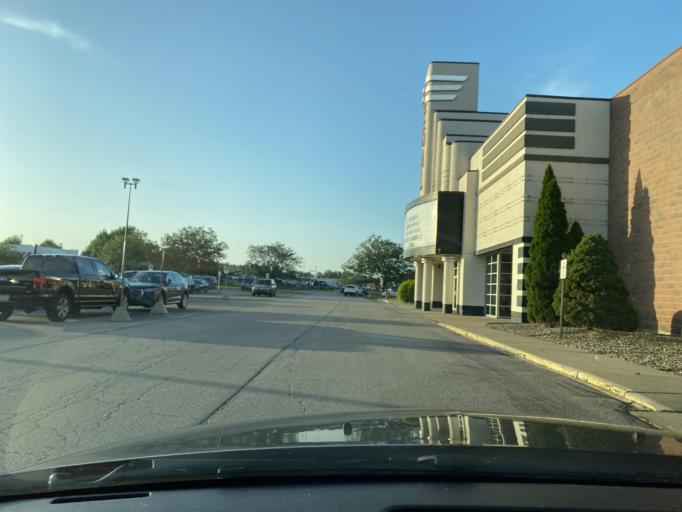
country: US
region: Ohio
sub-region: Summit County
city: Montrose-Ghent
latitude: 41.1325
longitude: -81.6422
